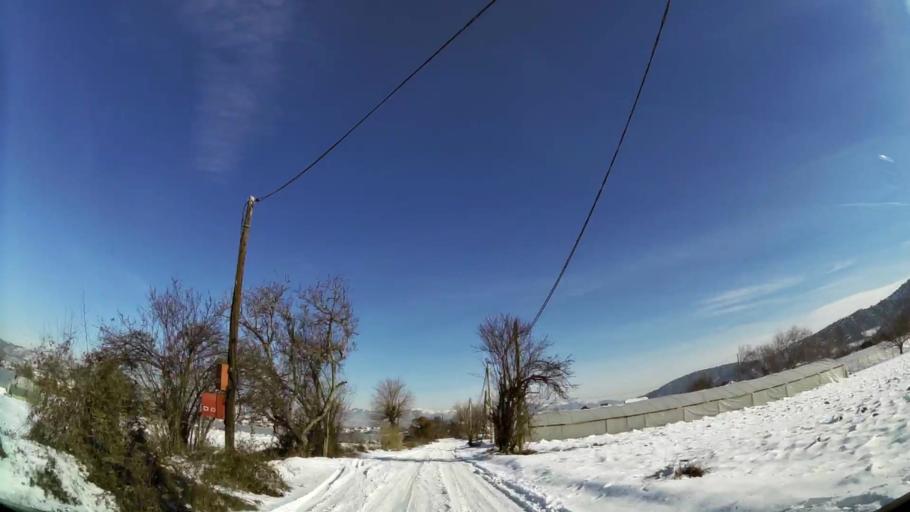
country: MK
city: Grchec
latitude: 41.9851
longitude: 21.3273
